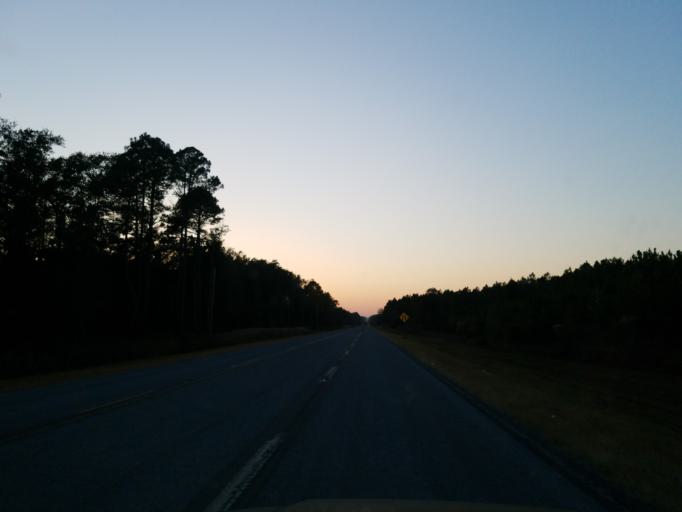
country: US
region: Georgia
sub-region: Ben Hill County
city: Fitzgerald
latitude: 31.7209
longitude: -83.4329
